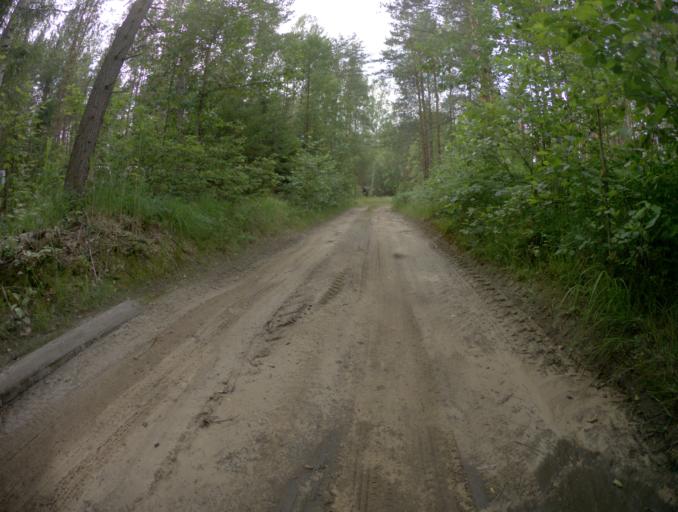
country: RU
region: Nizjnij Novgorod
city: Frolishchi
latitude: 56.3148
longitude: 42.6534
